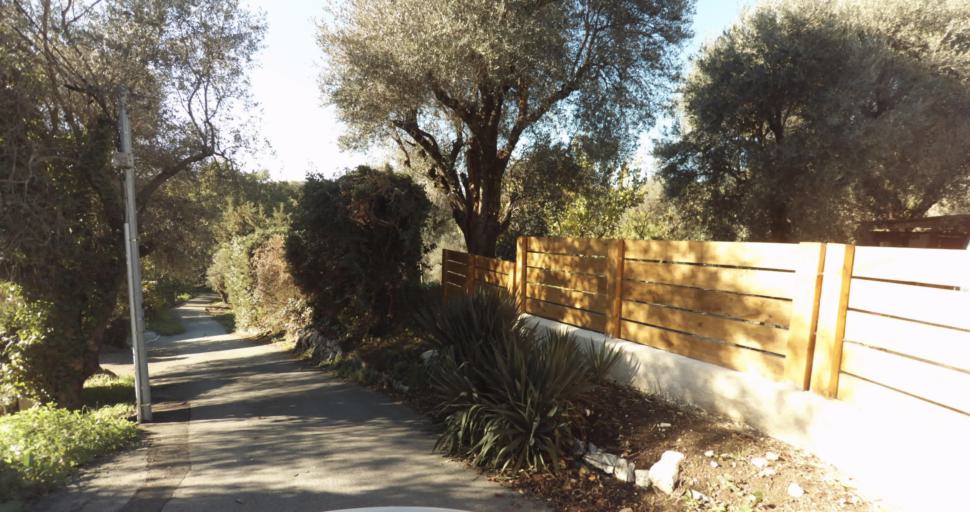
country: FR
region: Provence-Alpes-Cote d'Azur
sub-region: Departement des Alpes-Maritimes
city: Vence
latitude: 43.7144
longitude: 7.0842
